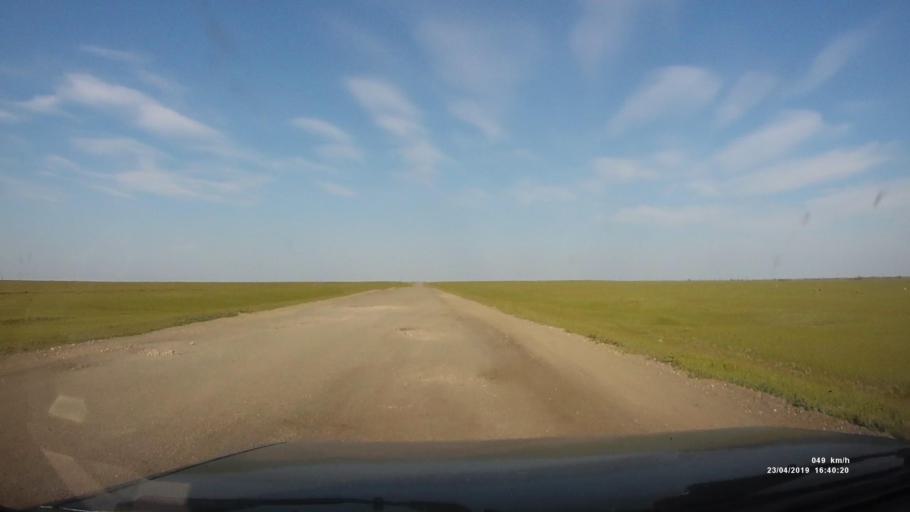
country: RU
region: Kalmykiya
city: Priyutnoye
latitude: 46.3426
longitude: 43.1756
